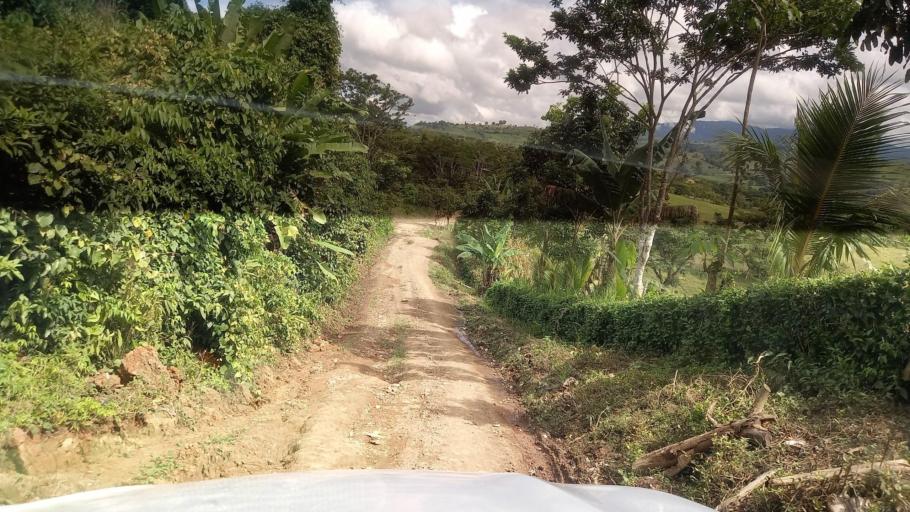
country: NI
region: Jinotega
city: San Jose de Bocay
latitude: 13.4068
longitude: -85.7020
